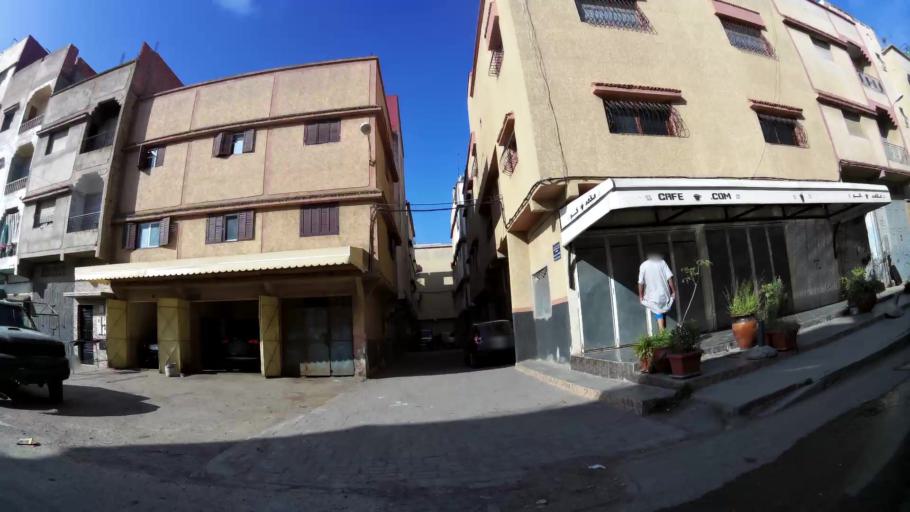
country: MA
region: Rabat-Sale-Zemmour-Zaer
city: Sale
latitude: 34.0514
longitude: -6.7747
